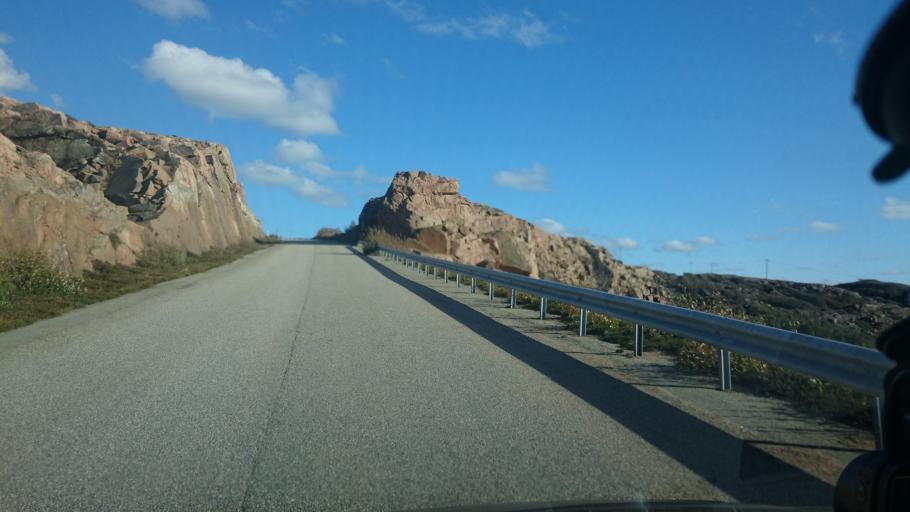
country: SE
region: Vaestra Goetaland
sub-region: Lysekils Kommun
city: Lysekil
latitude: 58.3169
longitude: 11.4048
